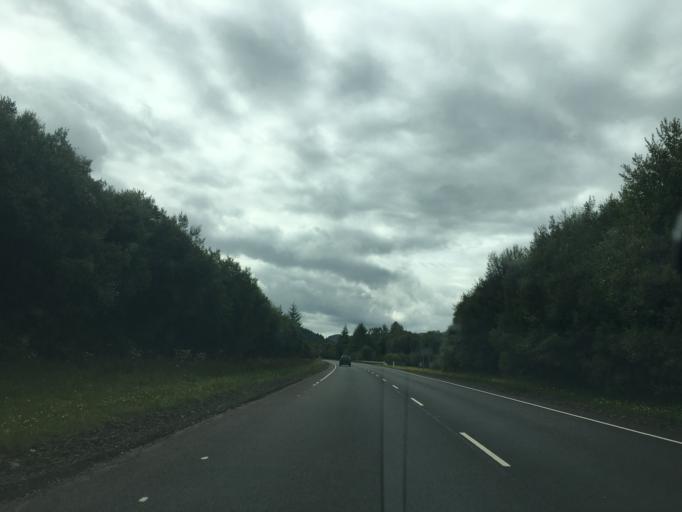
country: GB
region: Scotland
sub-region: Stirling
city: Callander
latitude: 56.3707
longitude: -4.2958
